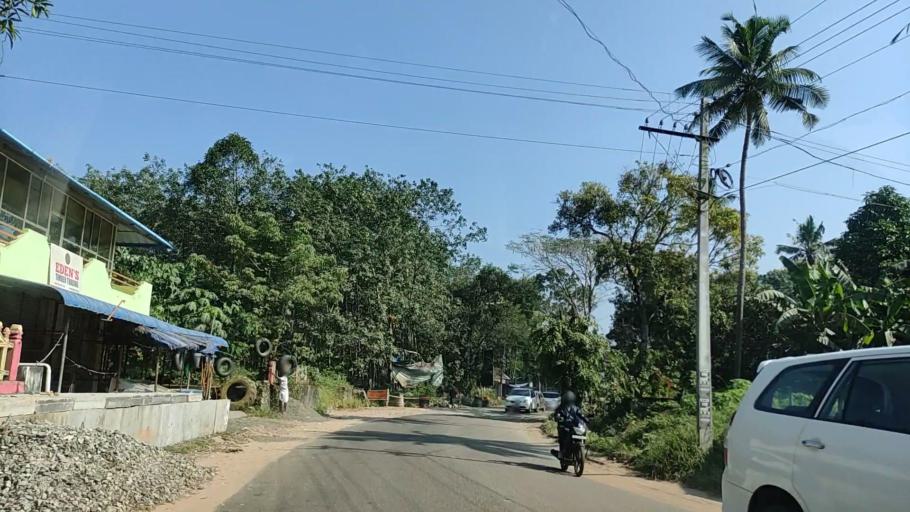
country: IN
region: Kerala
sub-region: Kollam
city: Punalur
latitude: 8.9067
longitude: 76.8761
